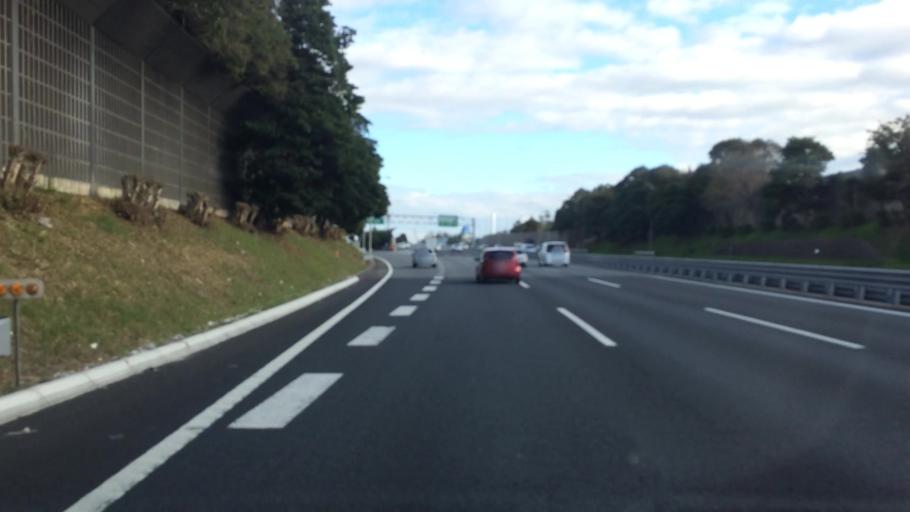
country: JP
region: Chiba
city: Chiba
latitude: 35.6568
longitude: 140.0978
